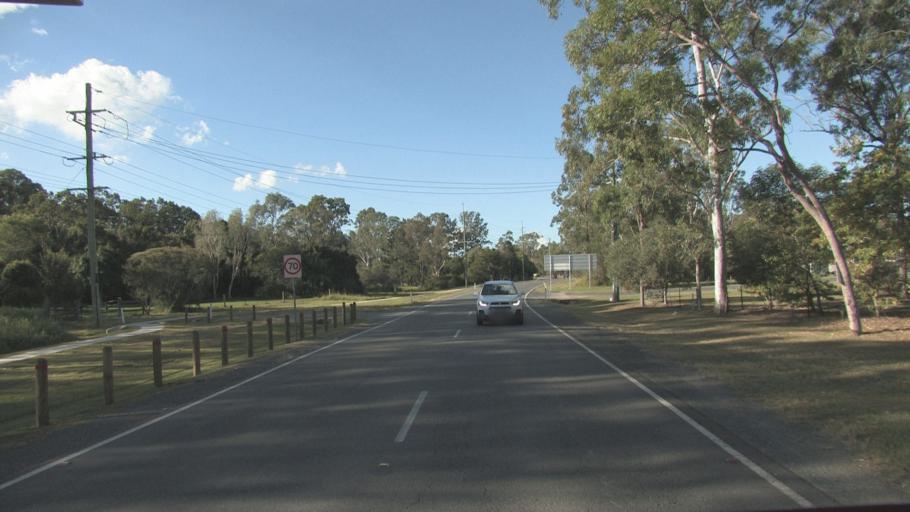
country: AU
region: Queensland
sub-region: Logan
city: Beenleigh
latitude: -27.6633
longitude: 153.2139
